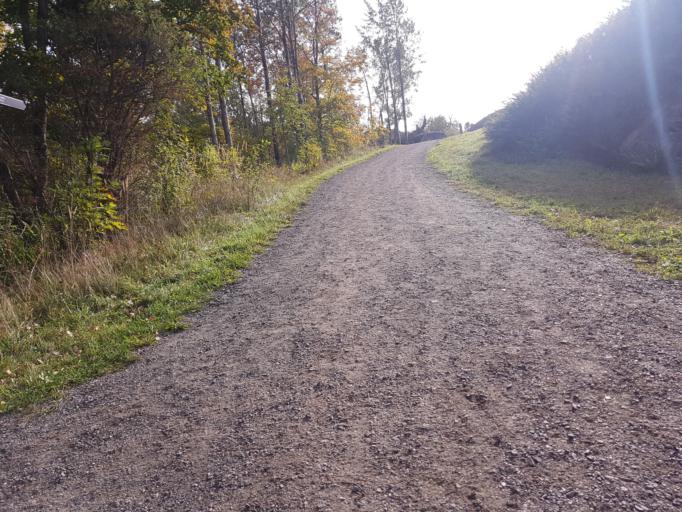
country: FI
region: Uusimaa
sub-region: Helsinki
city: Helsinki
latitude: 60.1373
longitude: 24.9961
